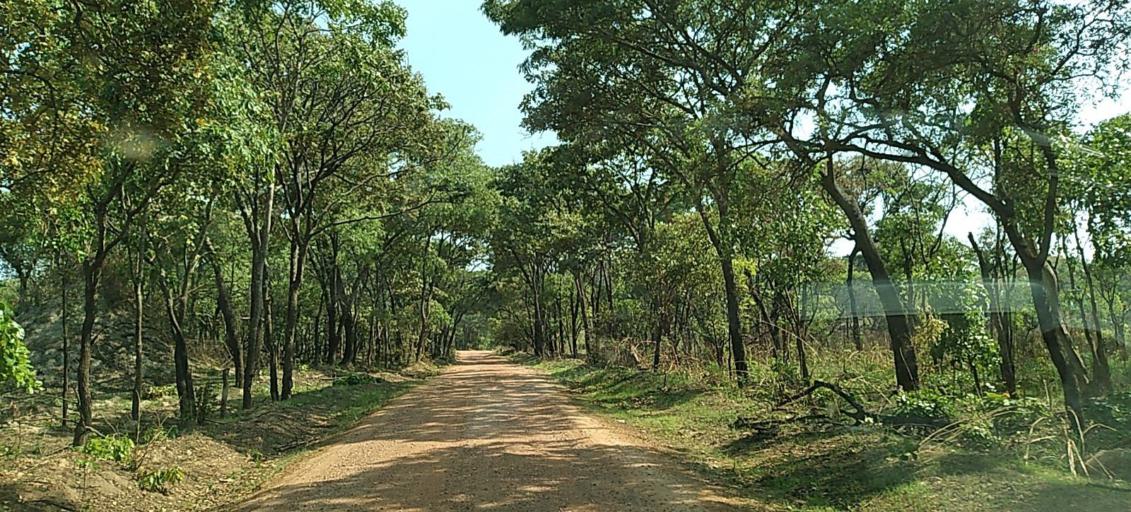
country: ZM
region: Copperbelt
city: Kalulushi
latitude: -12.9314
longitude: 27.8215
